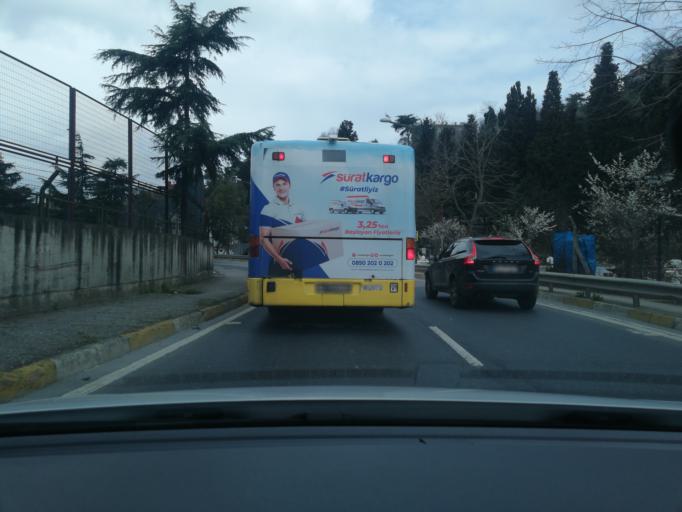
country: TR
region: Istanbul
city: UEskuedar
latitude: 41.0822
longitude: 29.0717
